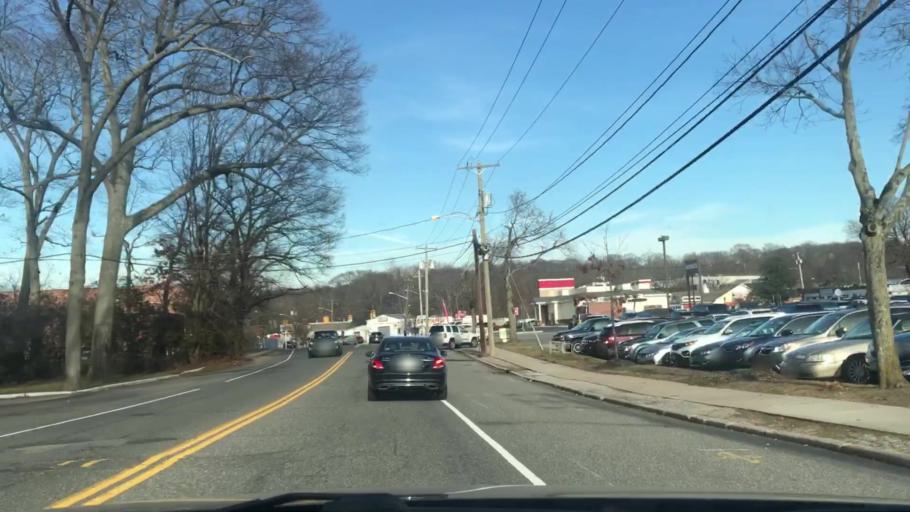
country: US
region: New York
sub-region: Suffolk County
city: Ronkonkoma
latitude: 40.8255
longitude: -73.1111
